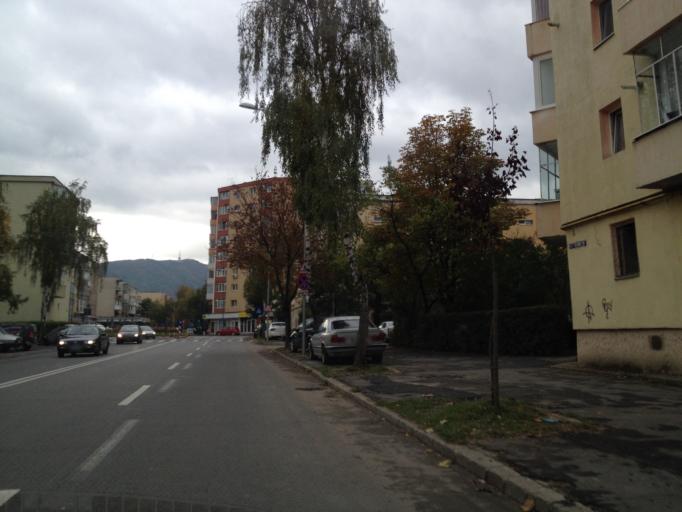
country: RO
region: Brasov
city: Brasov
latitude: 45.6673
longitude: 25.5990
